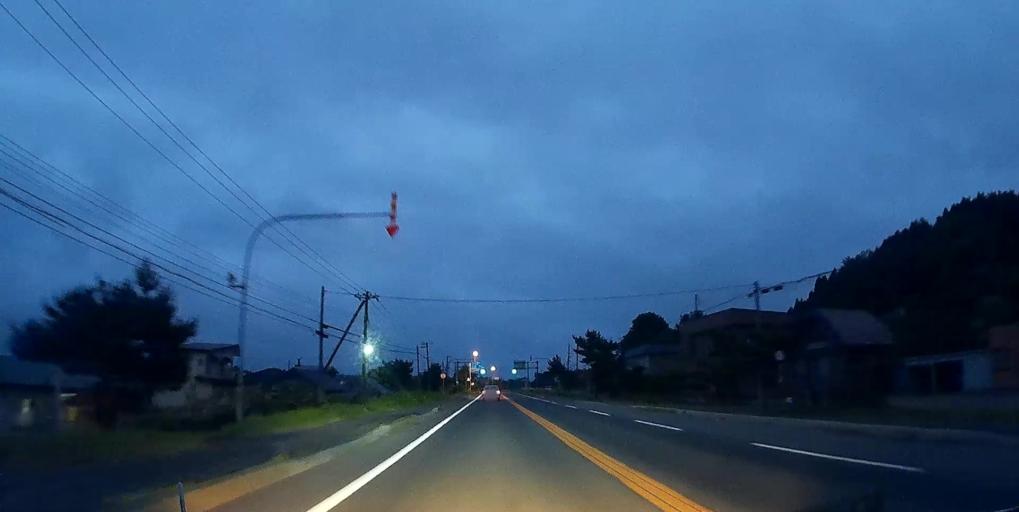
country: JP
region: Hokkaido
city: Nanae
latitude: 42.2221
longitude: 140.3690
